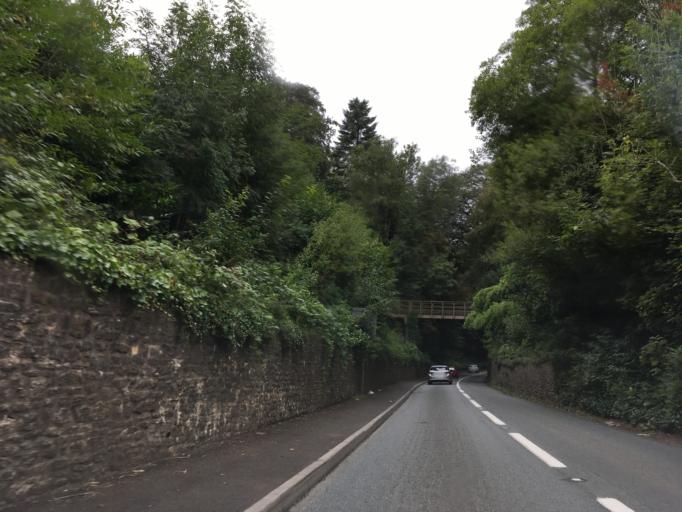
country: GB
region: England
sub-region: Bath and North East Somerset
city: Cameley
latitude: 51.2739
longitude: -2.5800
